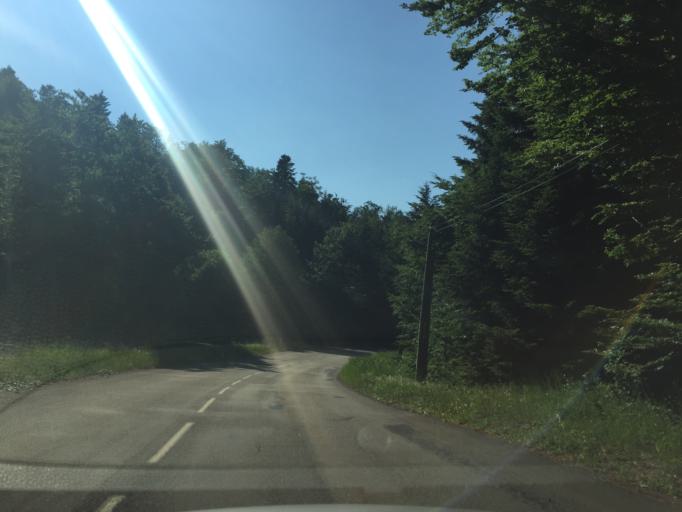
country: FR
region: Rhone-Alpes
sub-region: Departement de la Drome
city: Saint-Laurent-en-Royans
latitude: 44.9706
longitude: 5.3361
